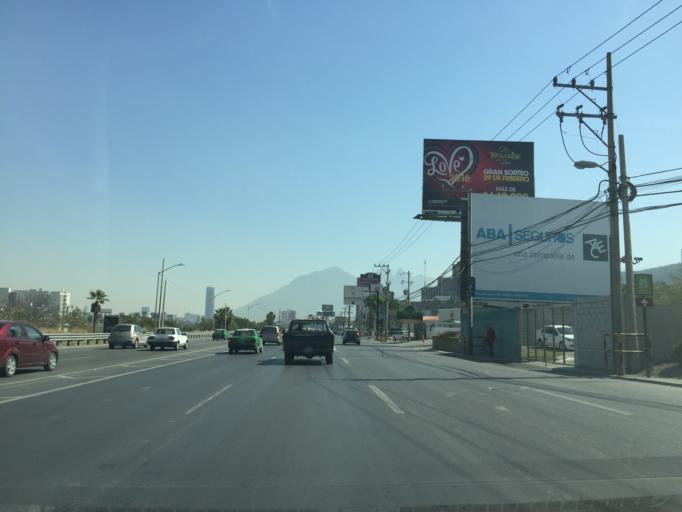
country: MX
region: Nuevo Leon
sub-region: Monterrey
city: Monterrey
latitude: 25.6692
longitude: -100.3482
